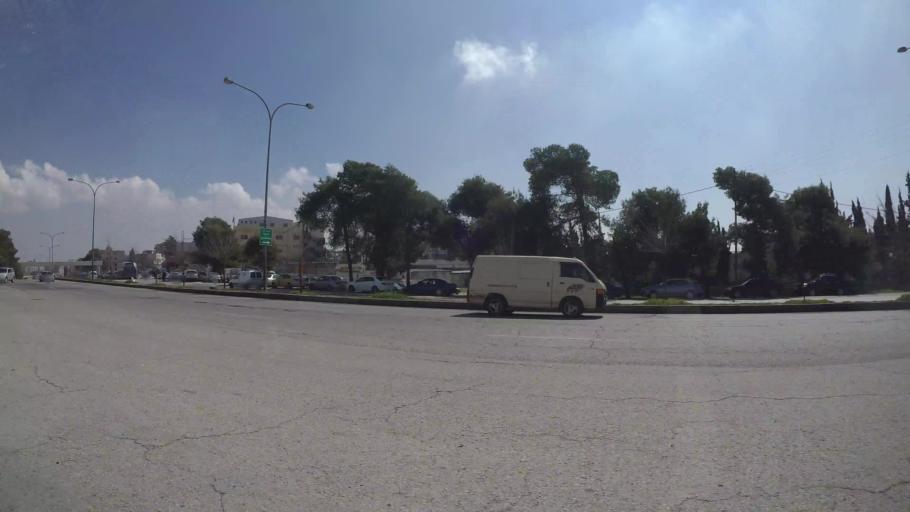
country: JO
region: Amman
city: Al Bunayyat ash Shamaliyah
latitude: 31.9101
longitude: 35.8902
